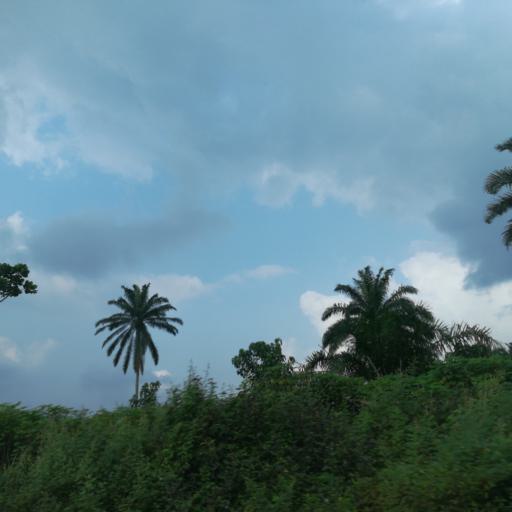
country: NG
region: Rivers
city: Okrika
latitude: 4.8257
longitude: 7.1253
